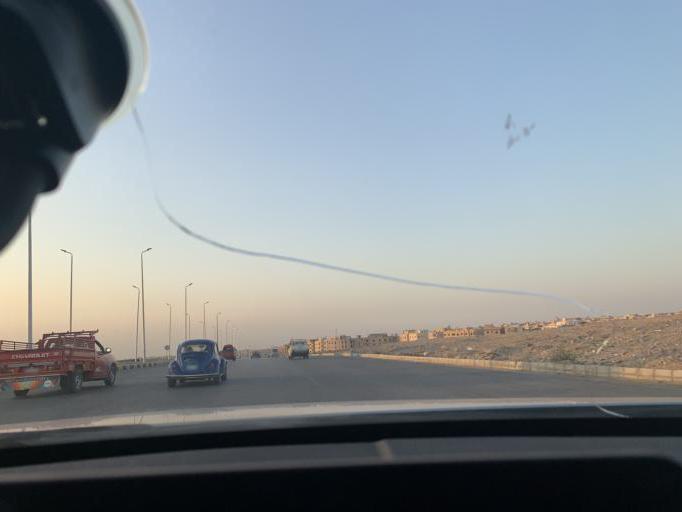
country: EG
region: Muhafazat al Qahirah
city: Halwan
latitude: 29.9883
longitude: 31.4689
